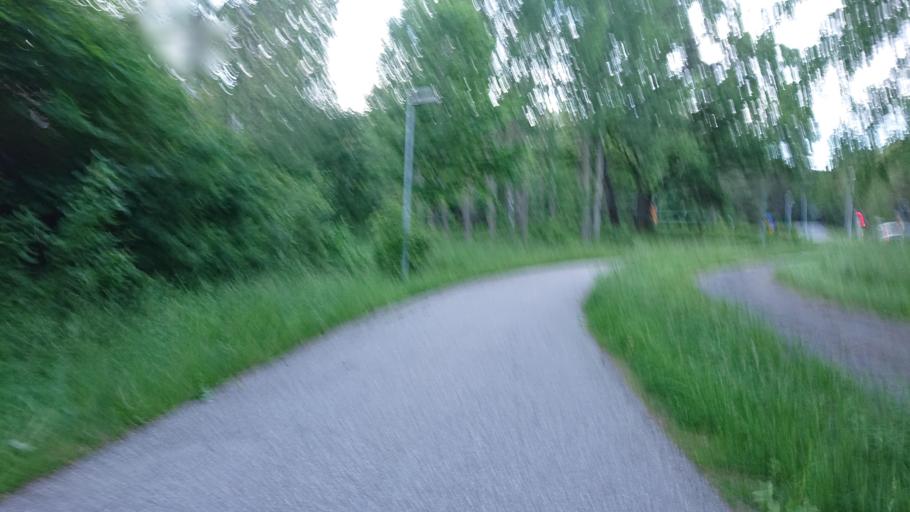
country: SE
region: Stockholm
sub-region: Osterakers Kommun
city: Akersberga
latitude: 59.5045
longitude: 18.3028
